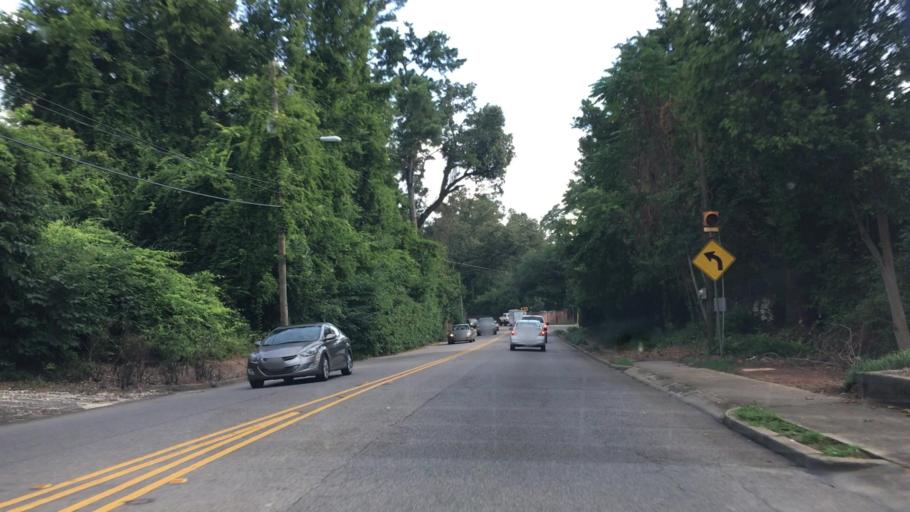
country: US
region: South Carolina
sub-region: Aiken County
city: Aiken
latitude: 33.5533
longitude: -81.7220
